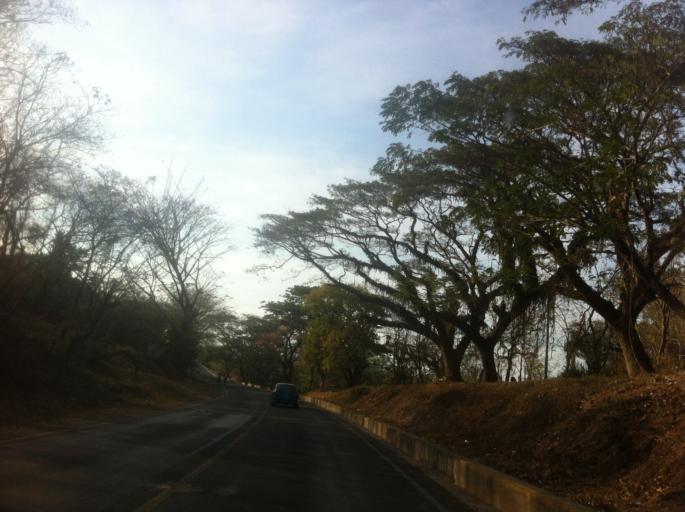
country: NI
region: Rivas
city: Cardenas
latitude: 11.2509
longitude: -85.6306
